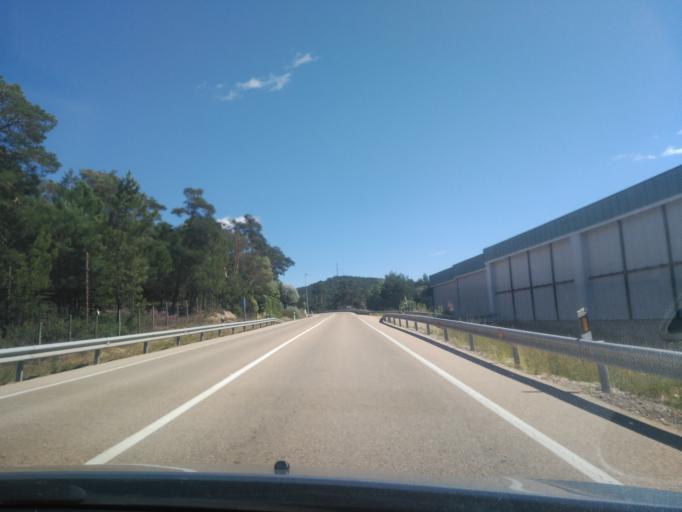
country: ES
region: Castille and Leon
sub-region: Provincia de Soria
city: Navaleno
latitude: 41.8388
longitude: -3.0169
